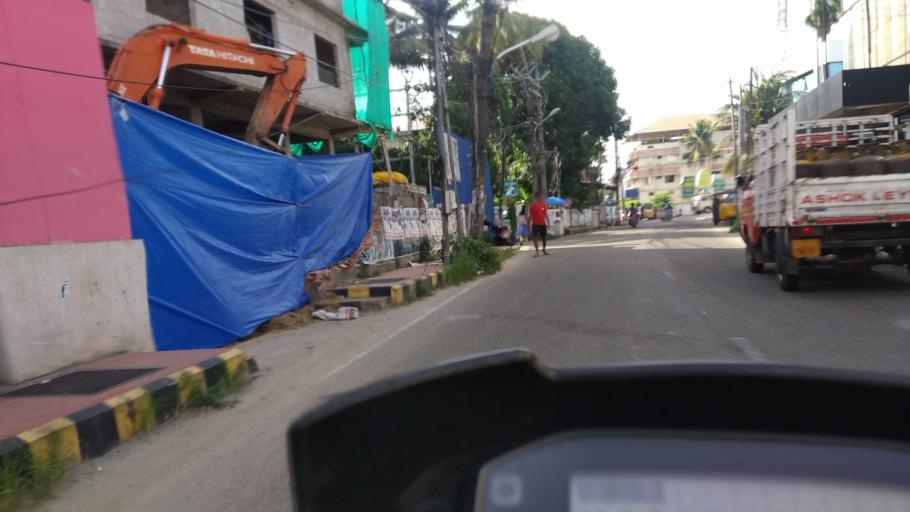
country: IN
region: Kerala
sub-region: Ernakulam
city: Elur
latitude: 10.0008
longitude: 76.2960
